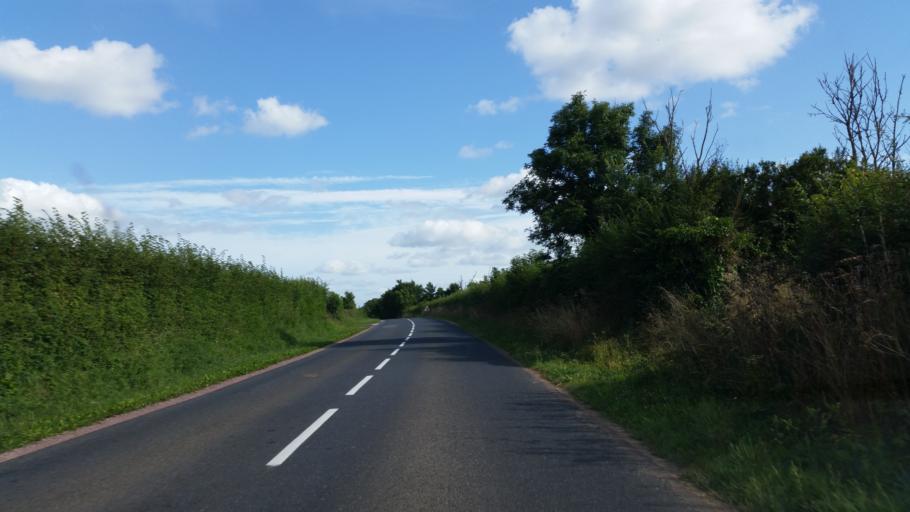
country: FR
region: Lower Normandy
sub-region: Departement de la Manche
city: Sainte-Mere-Eglise
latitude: 49.4506
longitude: -1.2643
